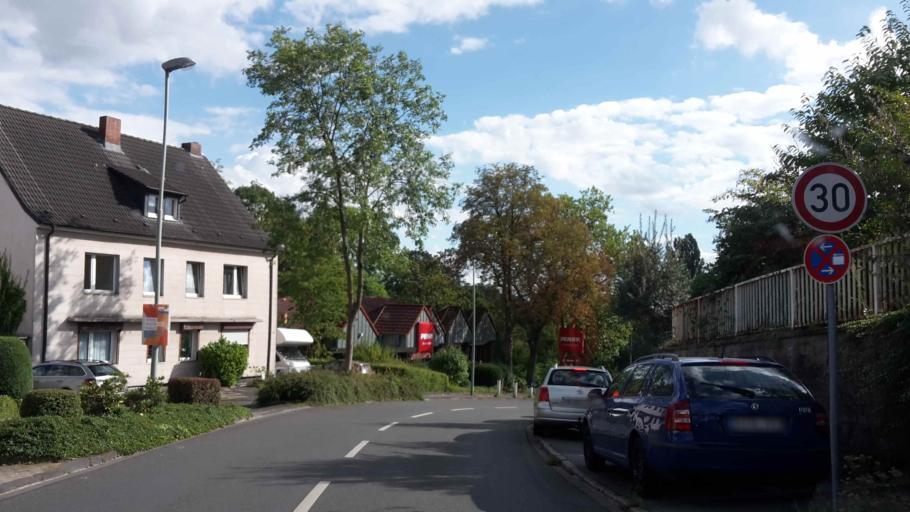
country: DE
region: North Rhine-Westphalia
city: Hattingen
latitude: 51.4380
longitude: 7.1583
